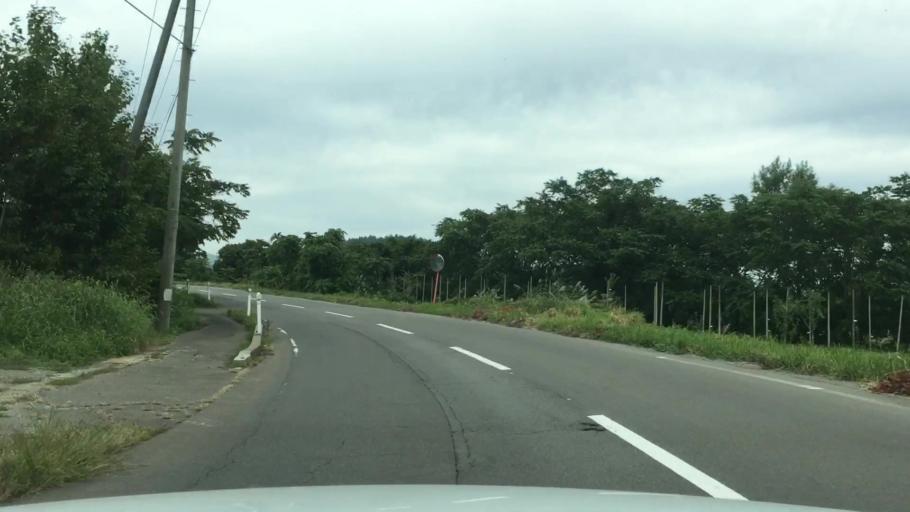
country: JP
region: Aomori
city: Hirosaki
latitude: 40.6671
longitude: 140.3988
